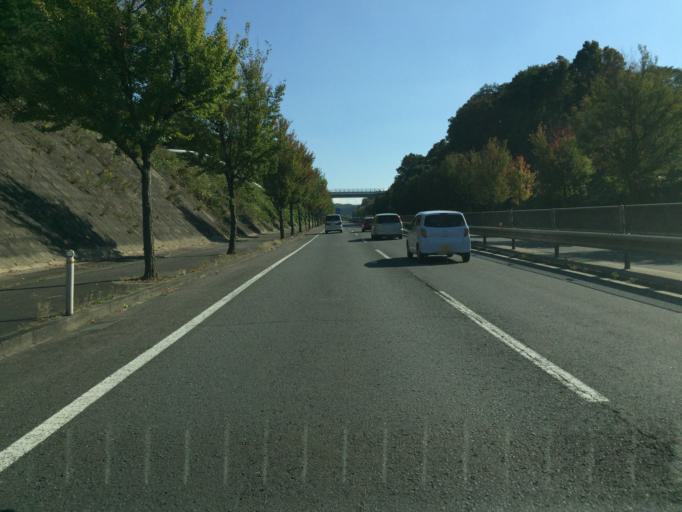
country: JP
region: Fukushima
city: Fukushima-shi
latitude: 37.6794
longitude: 140.4769
